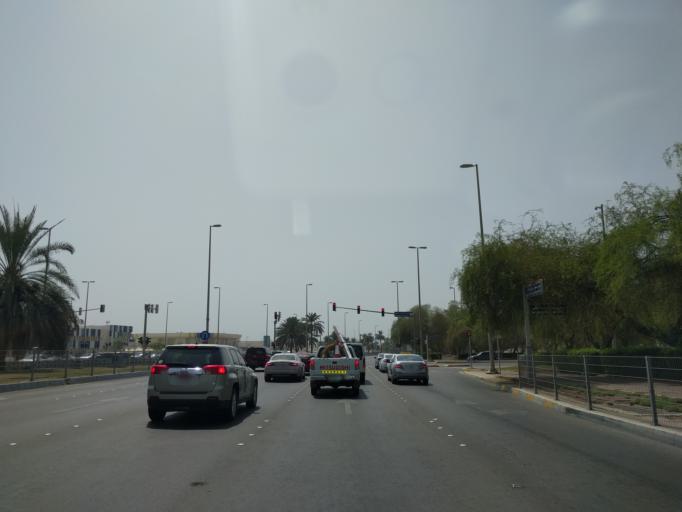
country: AE
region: Abu Dhabi
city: Abu Dhabi
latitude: 24.4413
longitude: 54.4079
